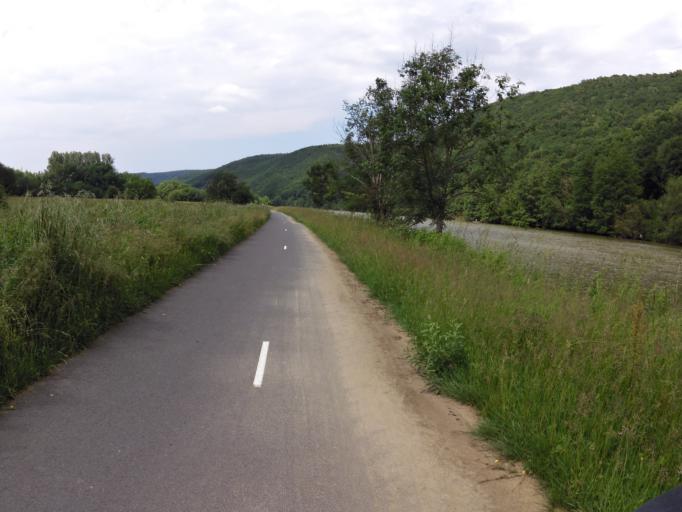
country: FR
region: Champagne-Ardenne
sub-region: Departement des Ardennes
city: Neufmanil
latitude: 49.8406
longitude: 4.7808
